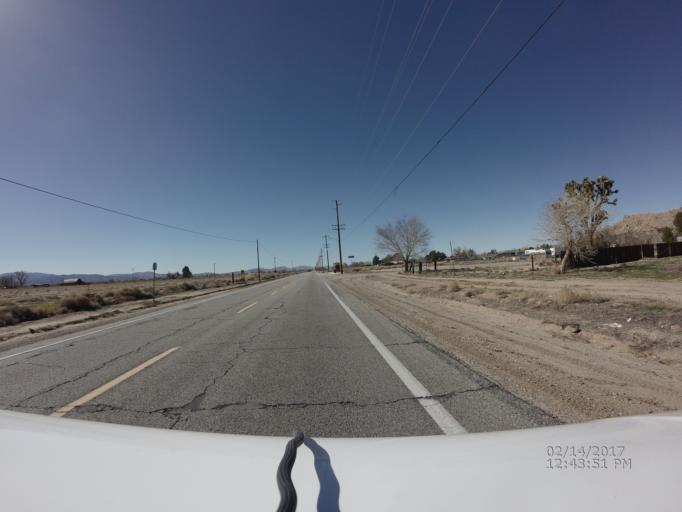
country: US
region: California
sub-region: Los Angeles County
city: Lake Los Angeles
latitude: 34.5798
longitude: -117.8484
